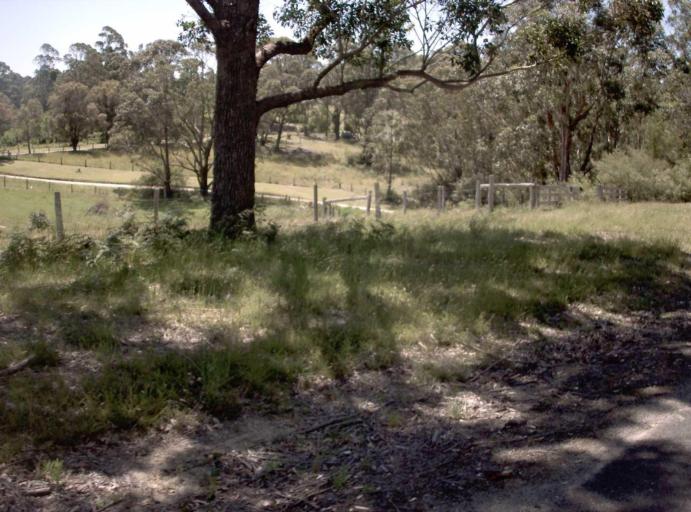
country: AU
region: Victoria
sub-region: East Gippsland
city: Lakes Entrance
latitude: -37.7323
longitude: 148.1099
